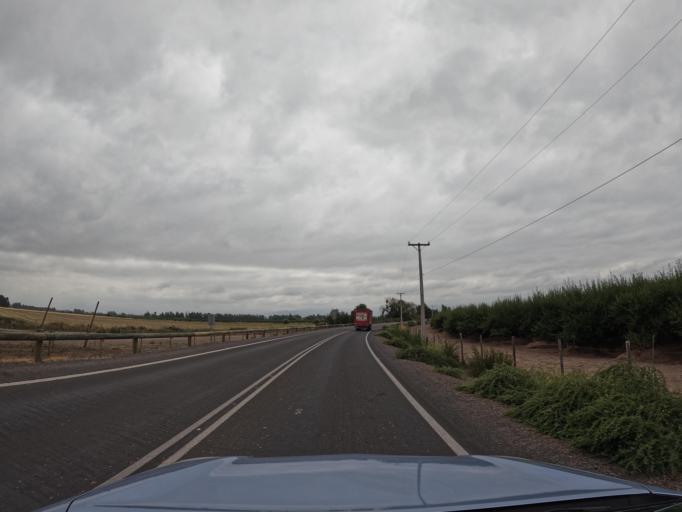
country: CL
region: O'Higgins
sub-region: Provincia de Colchagua
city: Chimbarongo
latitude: -34.7227
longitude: -71.0873
